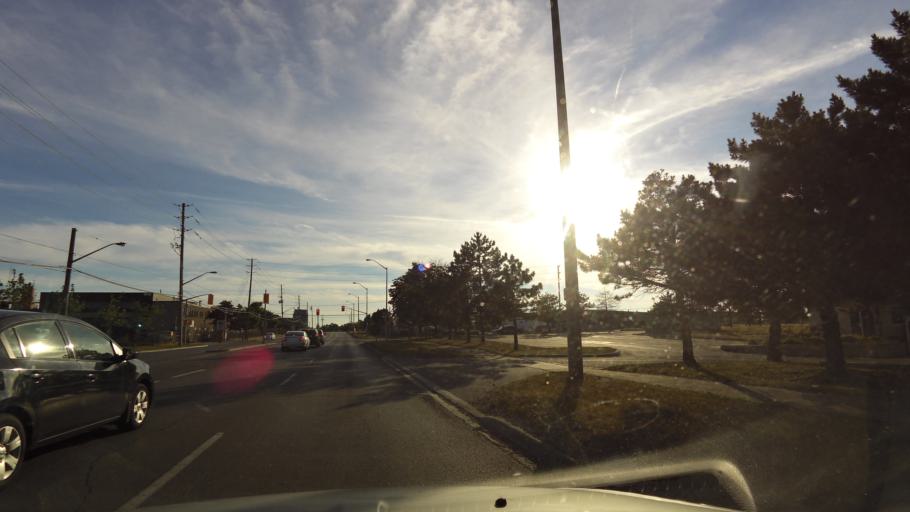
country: CA
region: Ontario
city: Brampton
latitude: 43.6940
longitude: -79.7389
